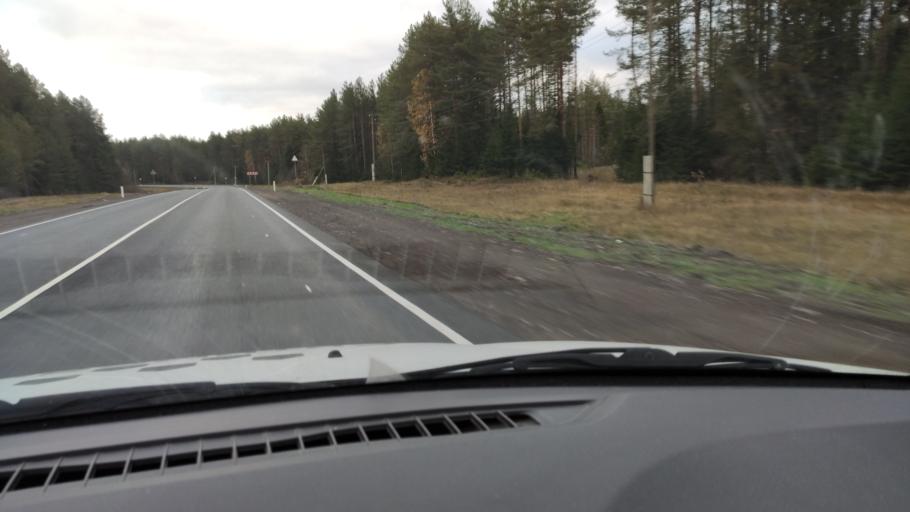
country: RU
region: Kirov
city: Belaya Kholunitsa
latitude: 58.8414
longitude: 50.7759
